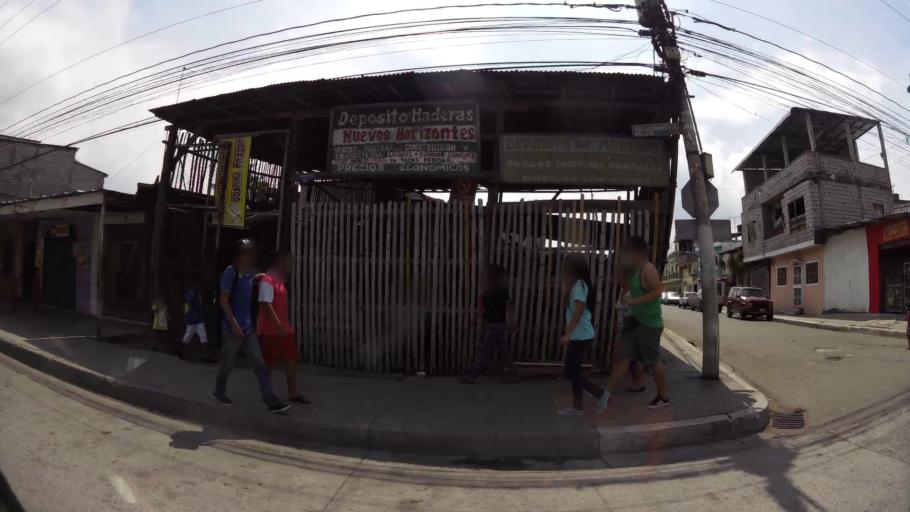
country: EC
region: Guayas
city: Guayaquil
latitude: -2.2600
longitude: -79.8826
